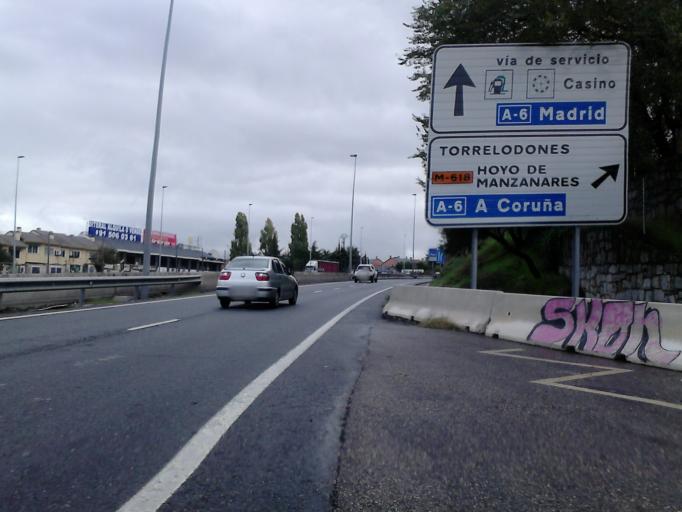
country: ES
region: Madrid
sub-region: Provincia de Madrid
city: Torrelodones
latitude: 40.5740
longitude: -3.9294
